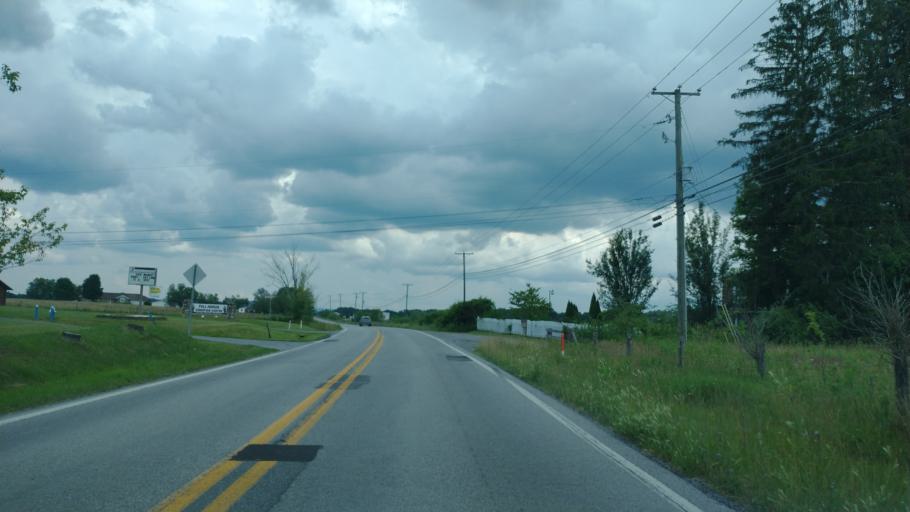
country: US
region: West Virginia
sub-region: Mercer County
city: Athens
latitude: 37.4552
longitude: -81.0097
